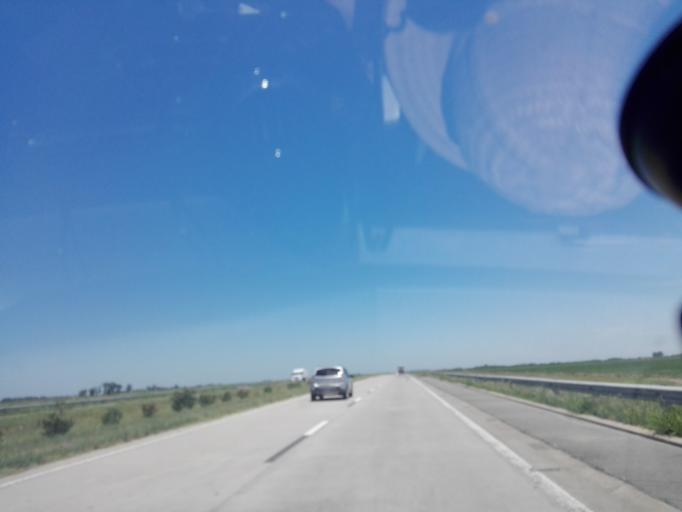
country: AR
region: Cordoba
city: Leones
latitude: -32.6143
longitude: -62.3813
